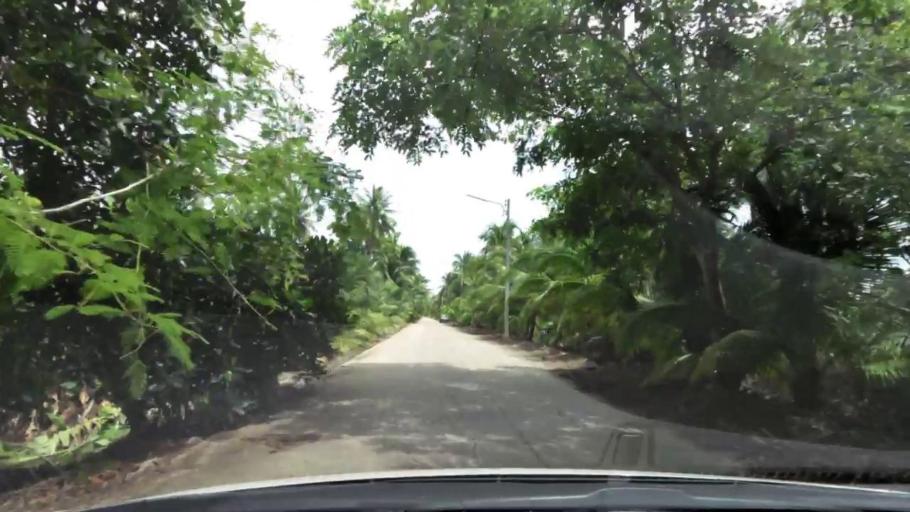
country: TH
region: Ratchaburi
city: Damnoen Saduak
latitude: 13.5272
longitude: 100.0033
